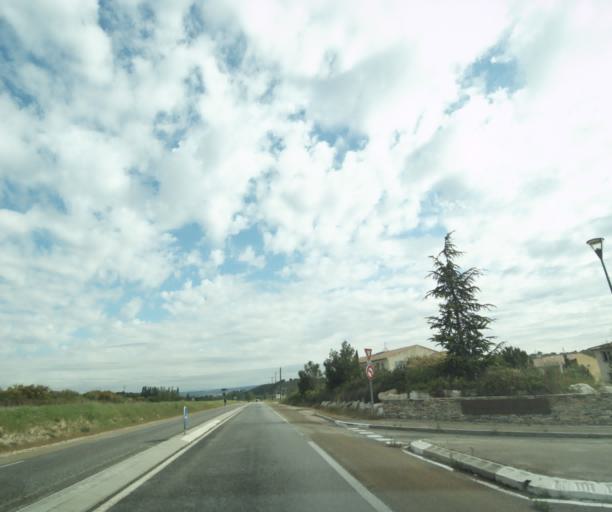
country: FR
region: Provence-Alpes-Cote d'Azur
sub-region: Departement des Bouches-du-Rhone
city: Cabries
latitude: 43.4687
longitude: 5.3543
